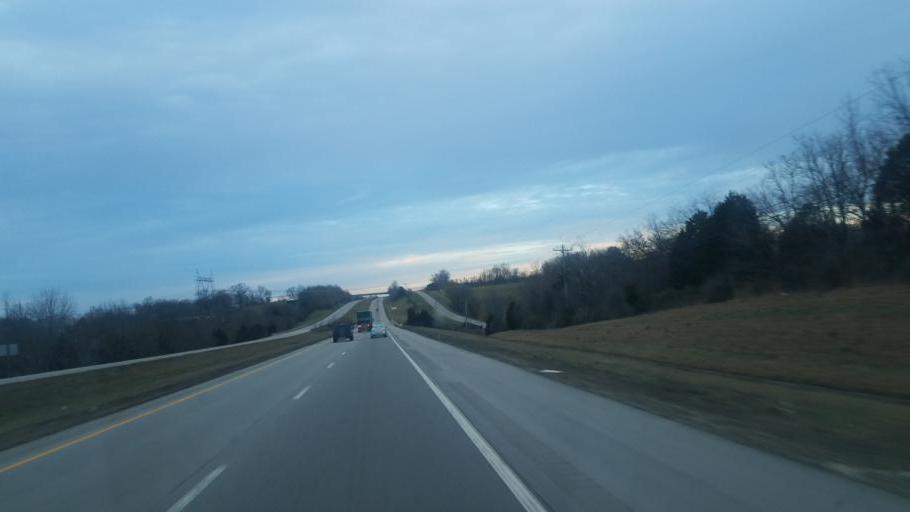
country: US
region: Tennessee
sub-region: Putnam County
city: Cookeville
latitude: 36.0645
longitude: -85.5072
